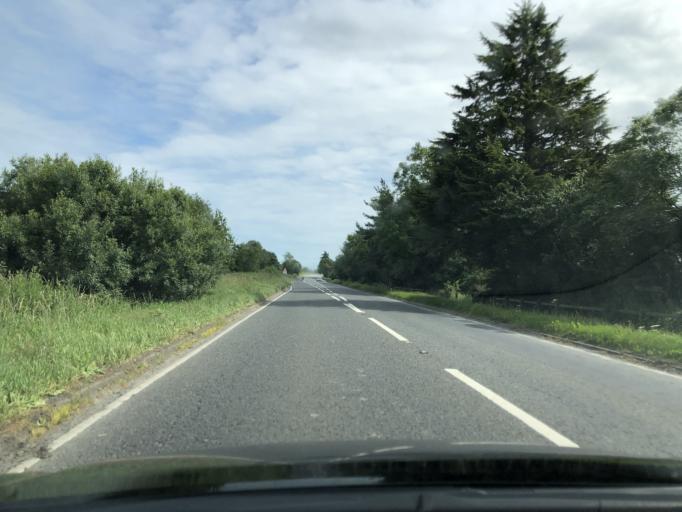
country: GB
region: Northern Ireland
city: Ballynahinch
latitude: 54.3415
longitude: -5.8421
